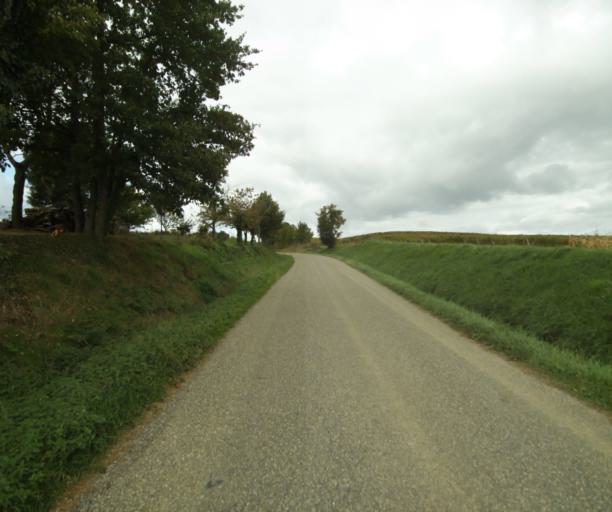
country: FR
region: Midi-Pyrenees
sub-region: Departement du Gers
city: Nogaro
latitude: 43.8228
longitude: -0.0217
